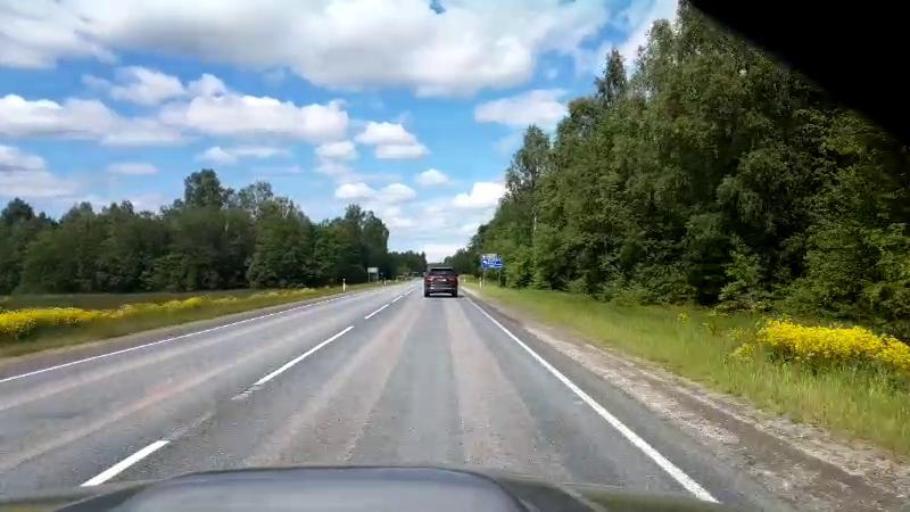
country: EE
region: Harju
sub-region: Saue linn
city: Saue
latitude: 59.1590
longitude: 24.5048
